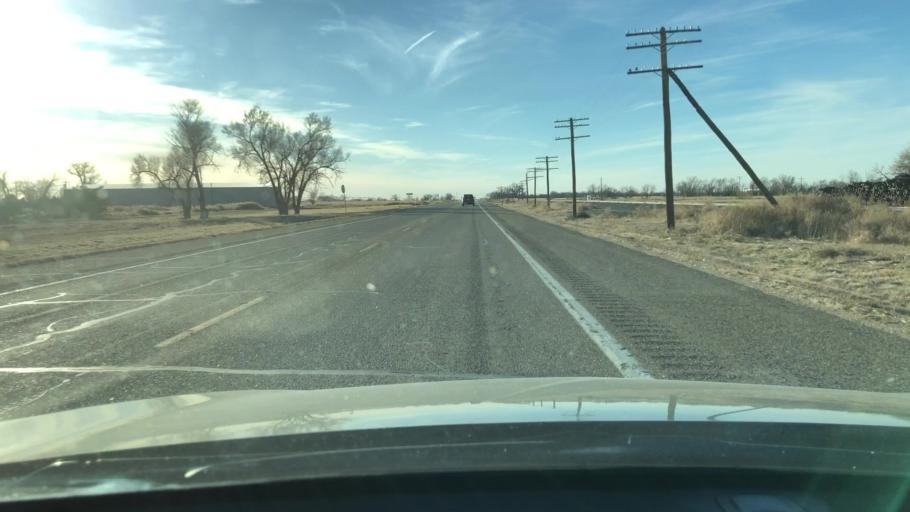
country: US
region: Colorado
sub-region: Prowers County
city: Lamar
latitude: 38.0862
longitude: -102.4169
